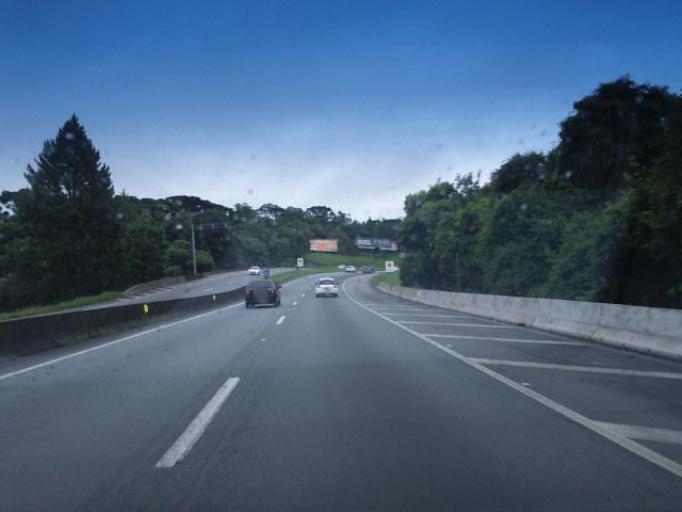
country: BR
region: Parana
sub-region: Sao Jose Dos Pinhais
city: Sao Jose dos Pinhais
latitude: -25.8452
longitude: -49.0614
